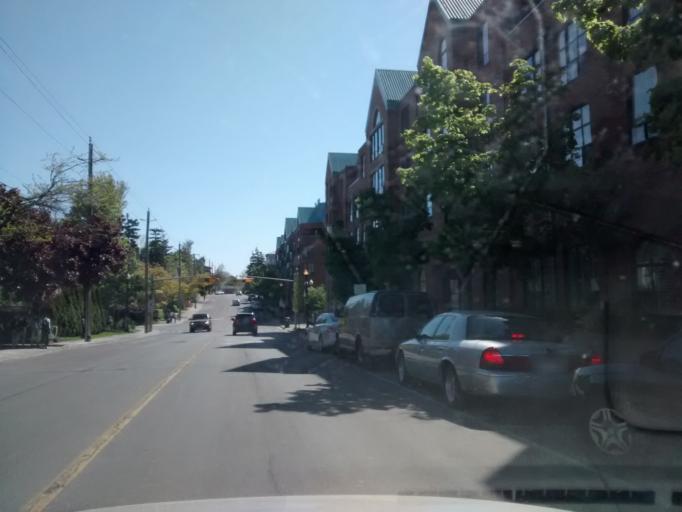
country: CA
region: Ontario
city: Oakville
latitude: 43.4458
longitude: -79.6668
